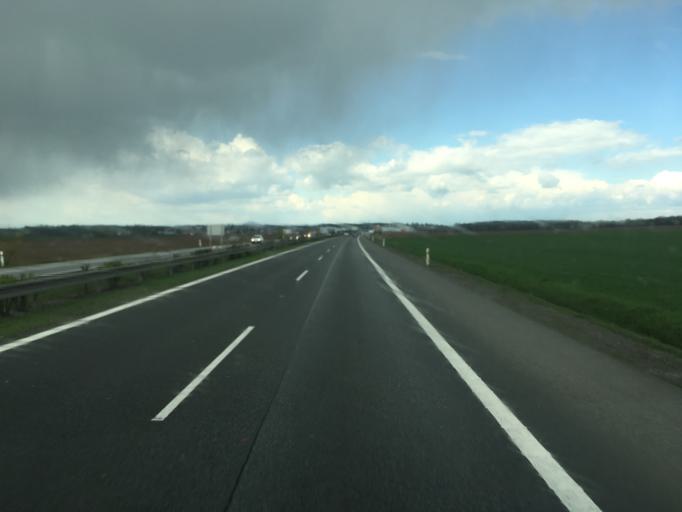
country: CZ
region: Central Bohemia
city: Zdiby
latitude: 50.1868
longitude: 14.4451
